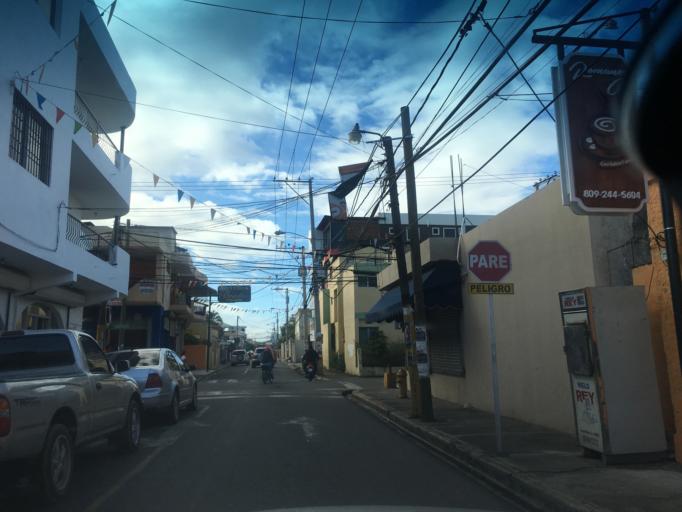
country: DO
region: Duarte
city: San Francisco de Macoris
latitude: 19.2955
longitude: -70.2583
